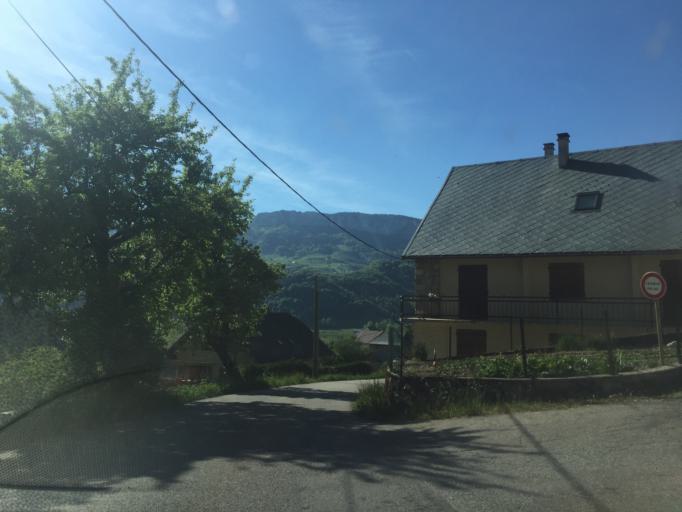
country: FR
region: Rhone-Alpes
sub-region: Departement de l'Isere
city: Barraux
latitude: 45.4491
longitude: 5.8939
